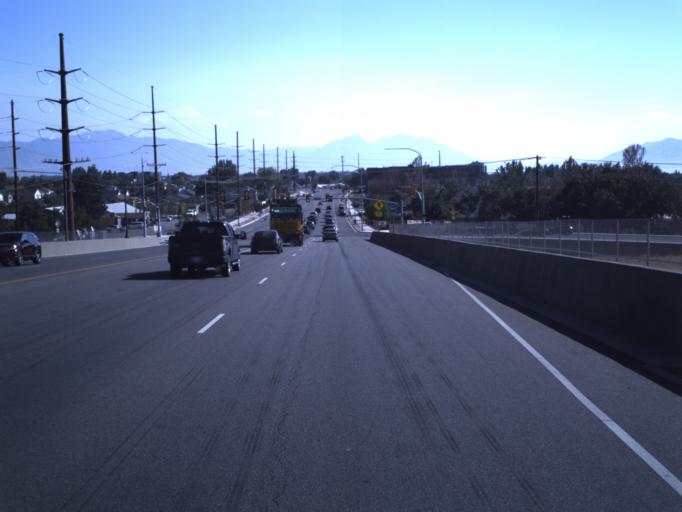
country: US
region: Utah
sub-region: Utah County
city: Orem
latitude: 40.2912
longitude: -111.7341
